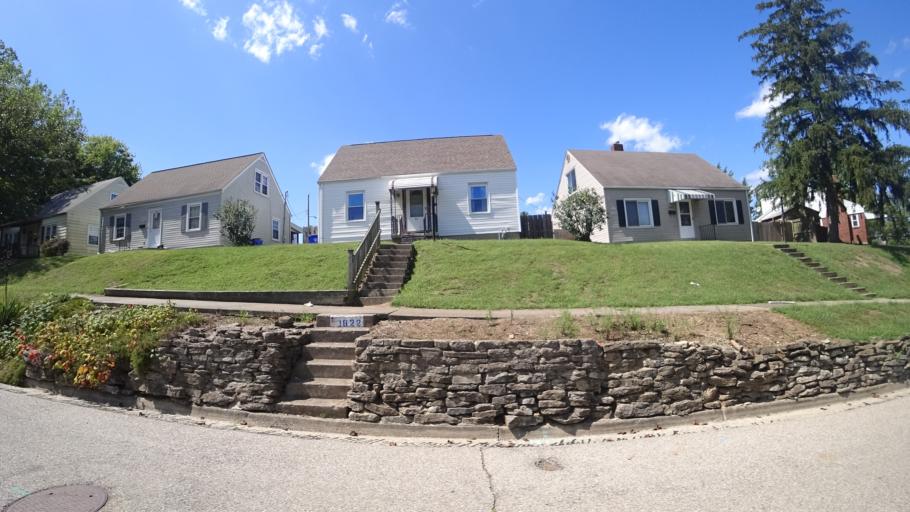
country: US
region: Ohio
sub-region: Butler County
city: New Miami
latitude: 39.4094
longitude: -84.5353
